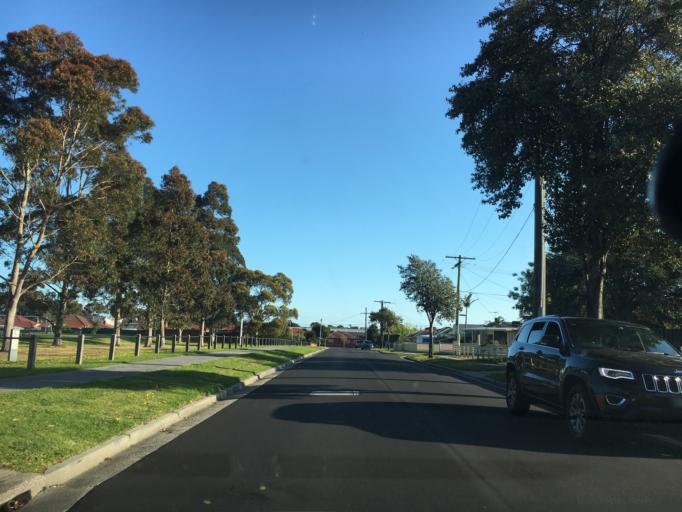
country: AU
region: Victoria
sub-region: Kingston
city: Clayton South
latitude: -37.9353
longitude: 145.1223
